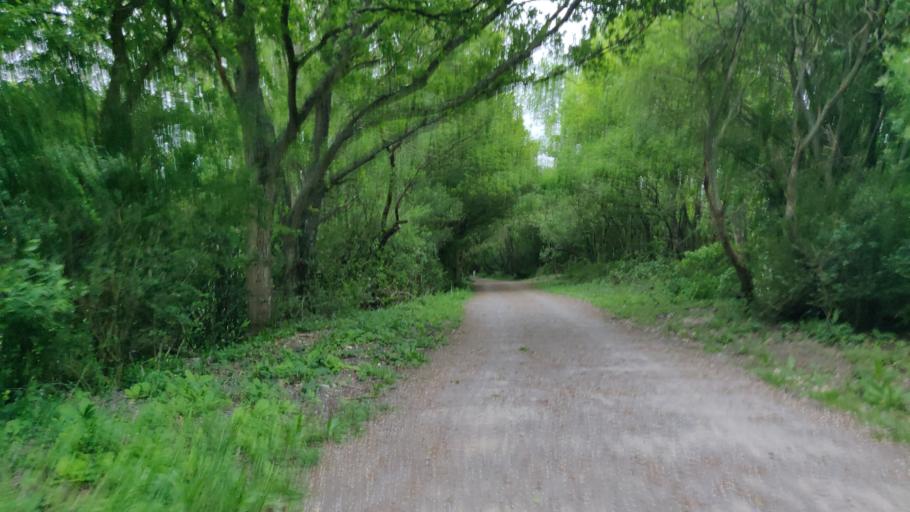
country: GB
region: England
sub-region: West Sussex
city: Partridge Green
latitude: 50.9644
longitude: -0.3141
